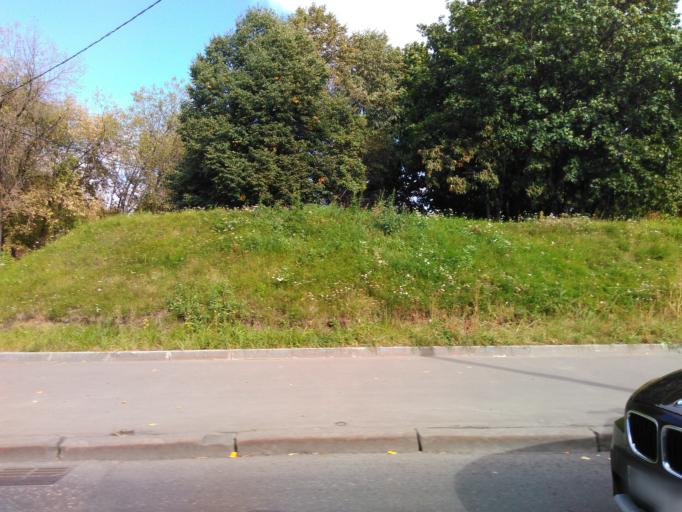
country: RU
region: Moscow
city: Sviblovo
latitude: 55.8449
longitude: 37.6361
